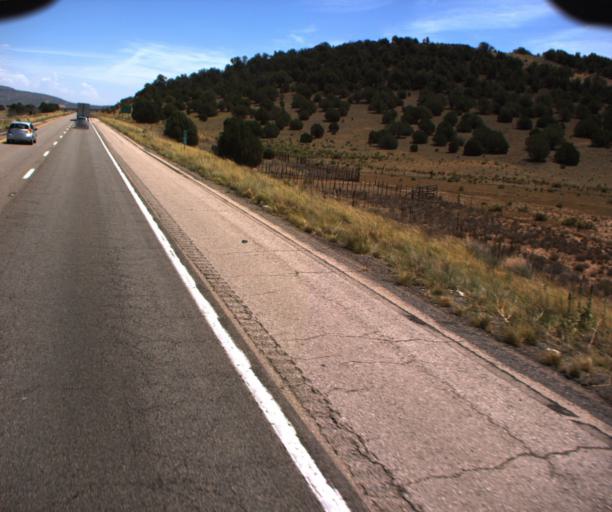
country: US
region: Arizona
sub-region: Mohave County
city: Peach Springs
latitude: 35.2466
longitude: -113.1883
